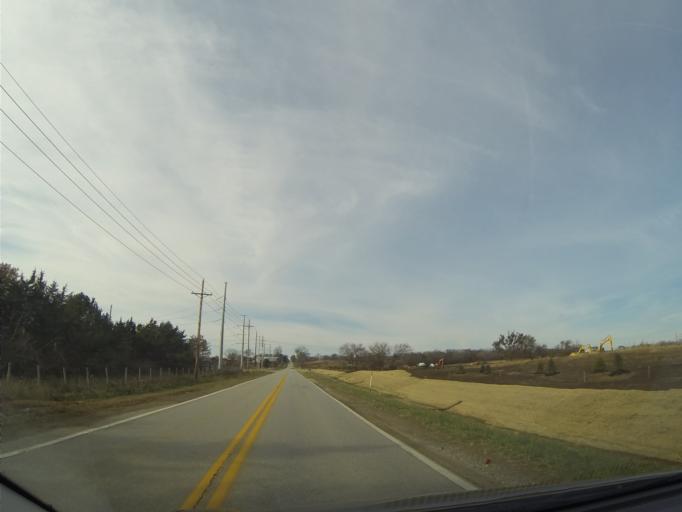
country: US
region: Nebraska
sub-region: Douglas County
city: Elkhorn
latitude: 41.2775
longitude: -96.2026
